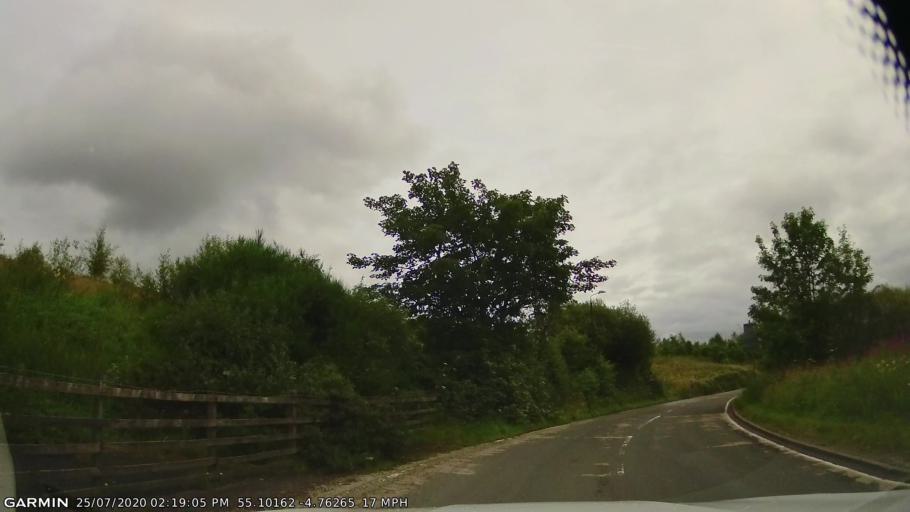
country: GB
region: Scotland
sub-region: South Ayrshire
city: Girvan
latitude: 55.1016
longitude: -4.7626
